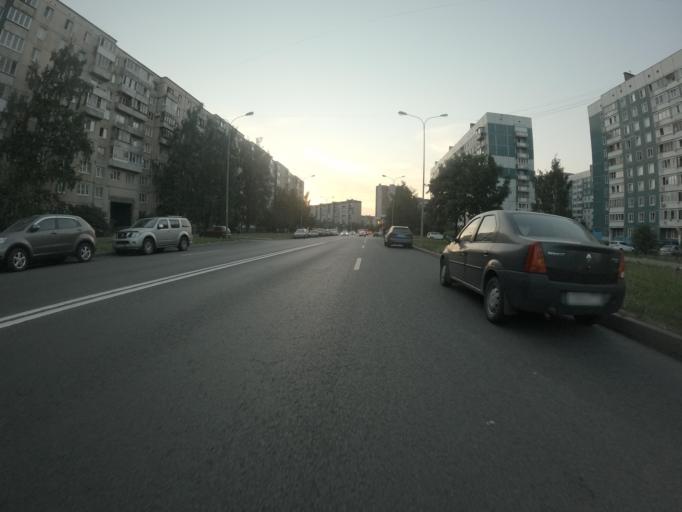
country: RU
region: St.-Petersburg
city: Krasnogvargeisky
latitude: 59.9149
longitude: 30.4583
